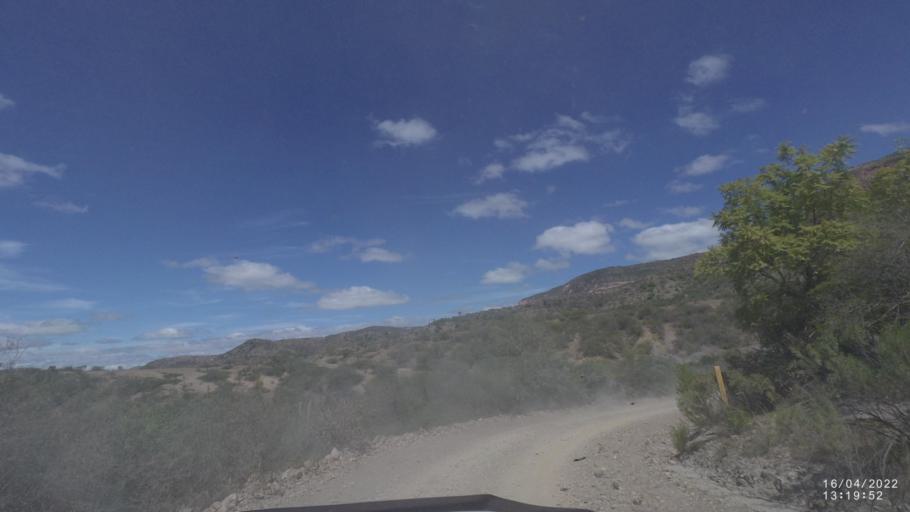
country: BO
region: Cochabamba
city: Mizque
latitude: -17.9887
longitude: -65.6142
